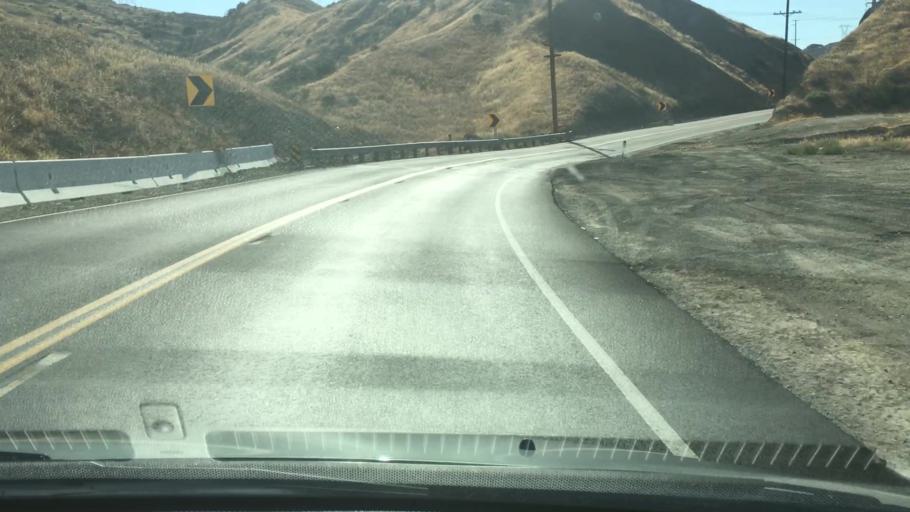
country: US
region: California
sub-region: Los Angeles County
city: Agua Dulce
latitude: 34.4748
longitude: -118.4485
